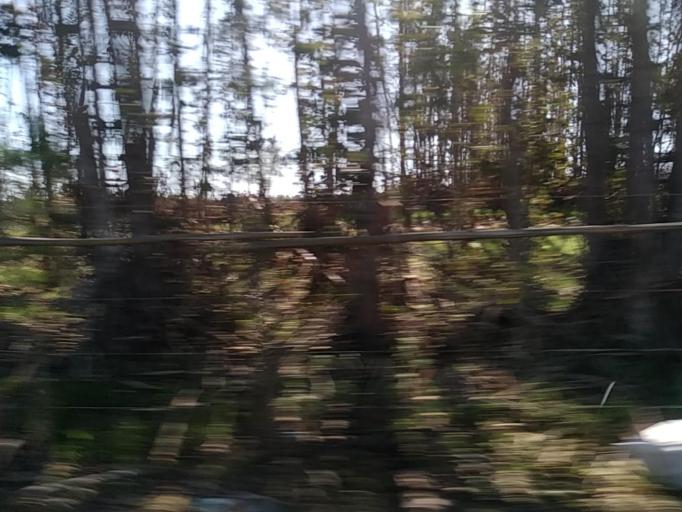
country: CL
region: Valparaiso
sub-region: San Antonio Province
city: El Tabo
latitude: -33.4102
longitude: -71.6050
